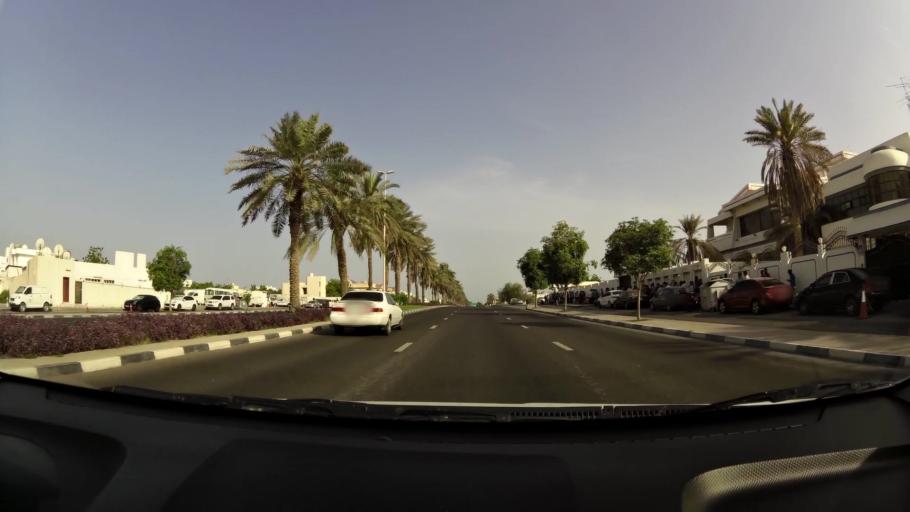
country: AE
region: Ash Shariqah
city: Sharjah
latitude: 25.2873
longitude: 55.3342
